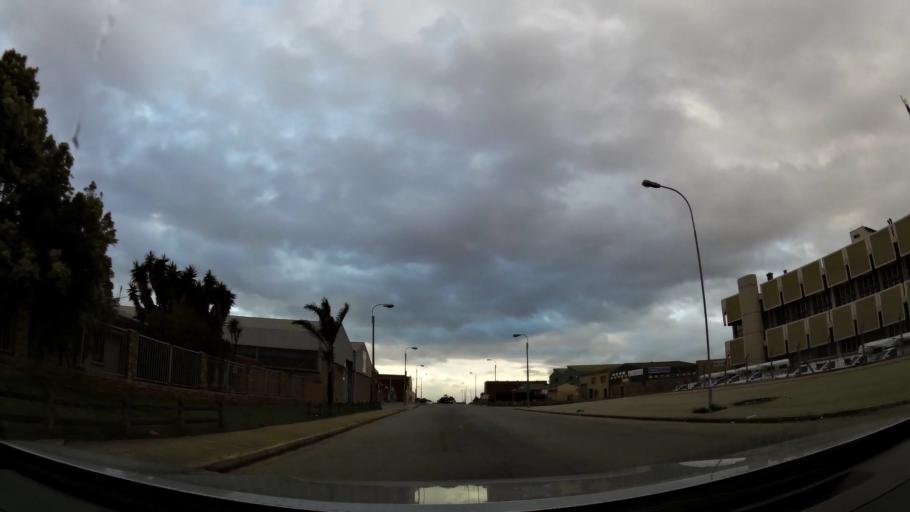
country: ZA
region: Eastern Cape
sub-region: Nelson Mandela Bay Metropolitan Municipality
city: Port Elizabeth
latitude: -33.9233
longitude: 25.5925
